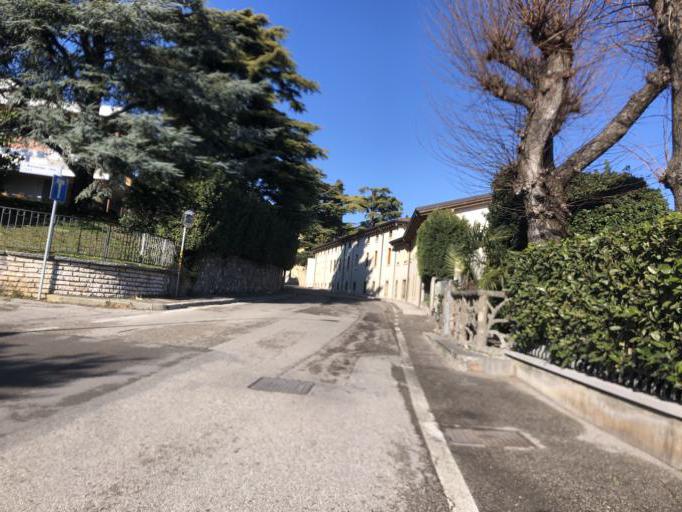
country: IT
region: Veneto
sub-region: Provincia di Verona
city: Sona
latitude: 45.4318
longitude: 10.8360
